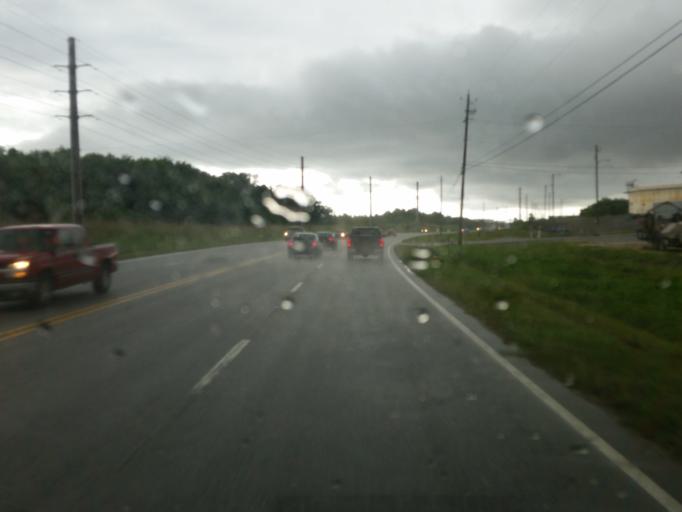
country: US
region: Alabama
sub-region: Mobile County
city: Mobile
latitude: 30.7163
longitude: -88.0342
